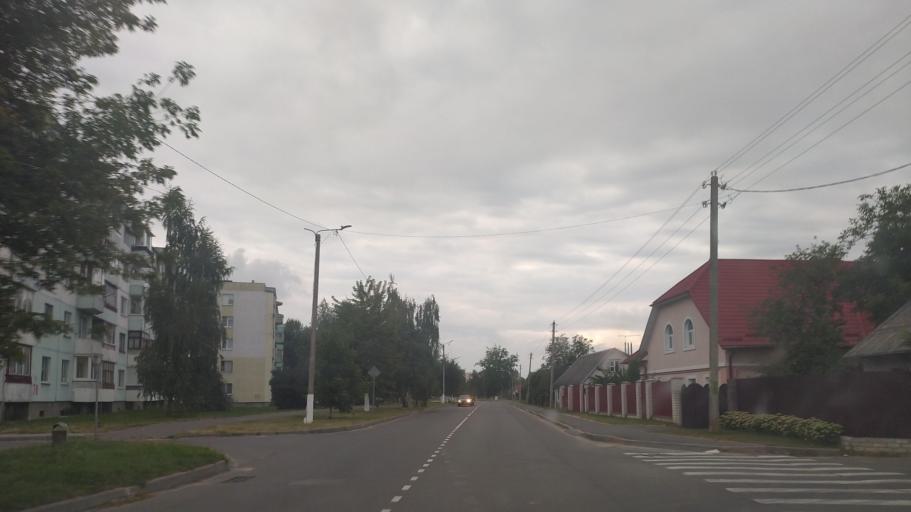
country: BY
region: Brest
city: Byaroza
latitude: 52.5288
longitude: 24.9878
